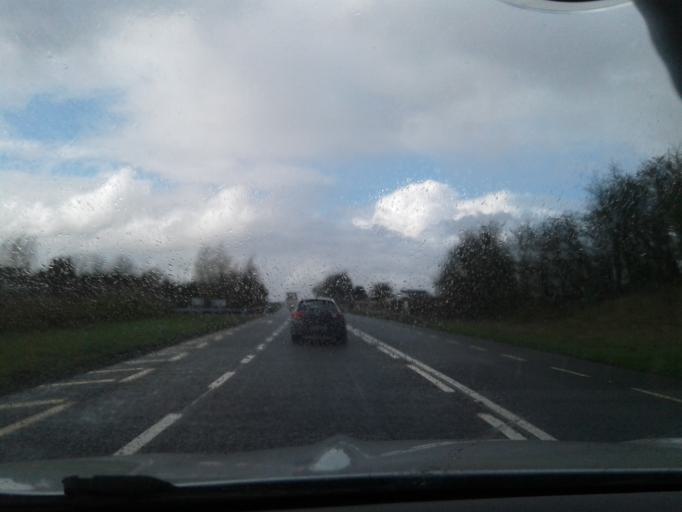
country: IE
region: Ulster
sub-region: County Monaghan
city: Carrickmacross
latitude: 53.9334
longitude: -6.6523
